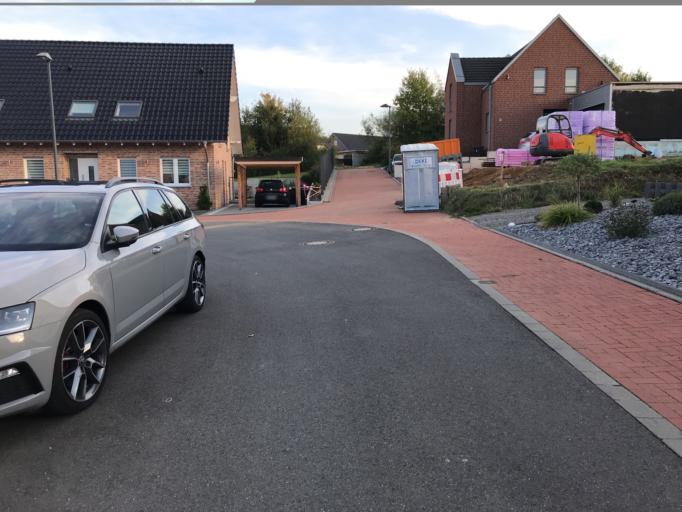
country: DE
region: North Rhine-Westphalia
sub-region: Regierungsbezirk Koln
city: Langerwehe
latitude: 50.8215
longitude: 6.3490
